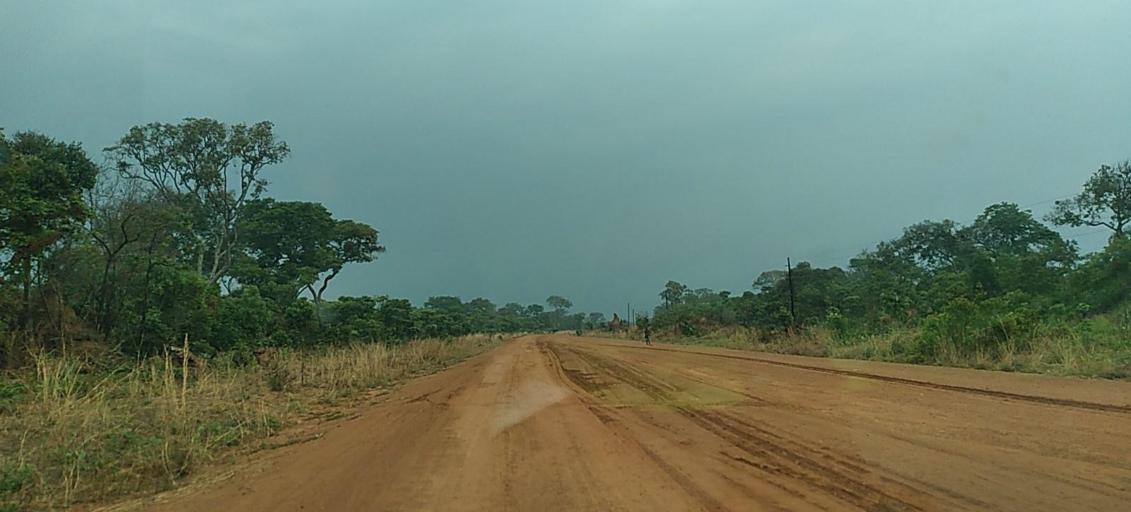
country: ZM
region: North-Western
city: Mwinilunga
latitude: -11.6314
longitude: 24.4017
